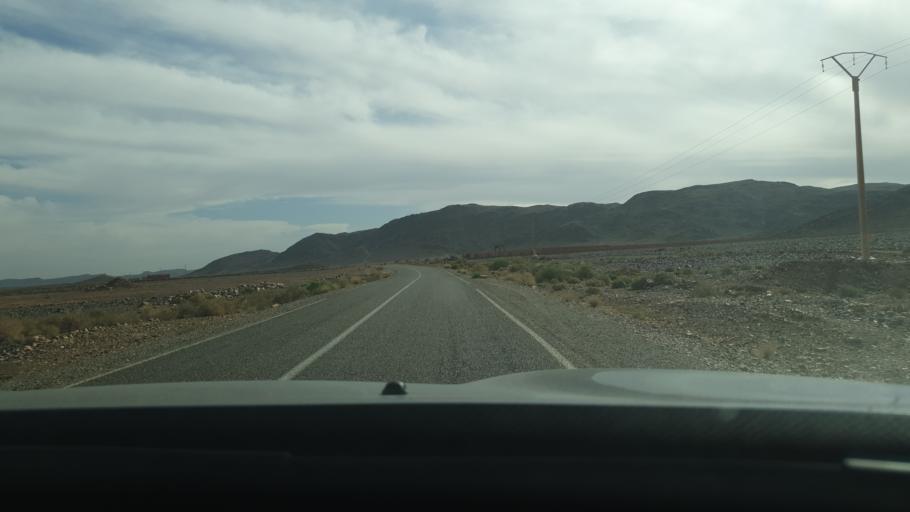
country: MA
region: Meknes-Tafilalet
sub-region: Errachidia
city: Fezna
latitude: 31.5300
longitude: -4.6386
